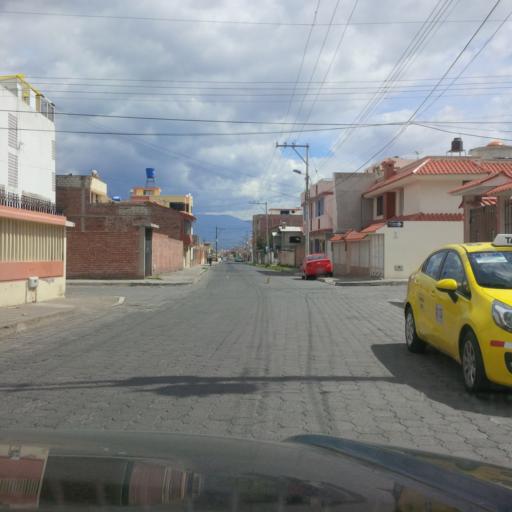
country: EC
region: Chimborazo
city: Riobamba
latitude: -1.6475
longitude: -78.6673
